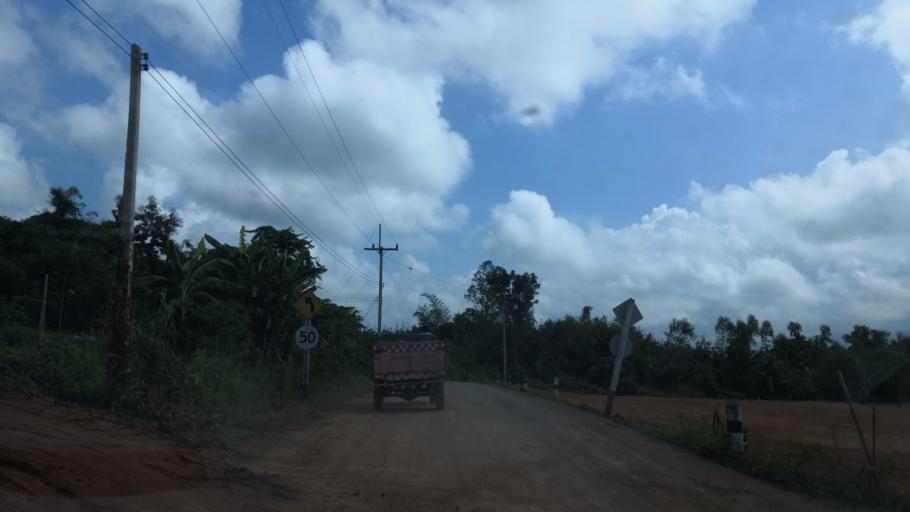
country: TH
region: Chiang Rai
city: Wiang Chiang Rung
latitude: 20.0203
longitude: 100.0427
